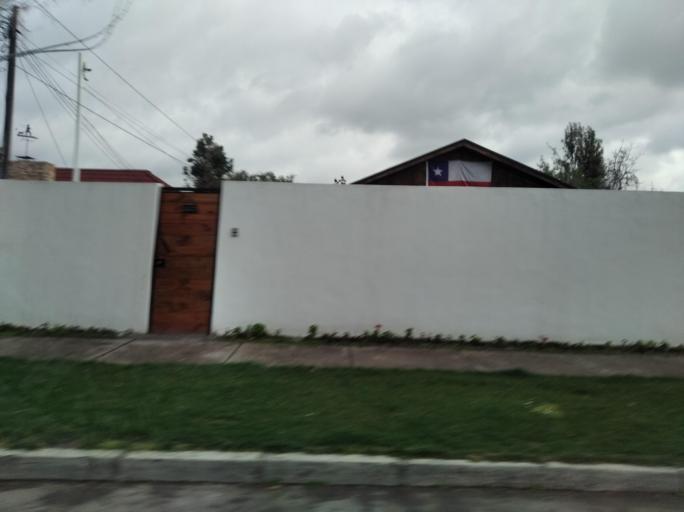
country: CL
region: Santiago Metropolitan
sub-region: Provincia de Santiago
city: Villa Presidente Frei, Nunoa, Santiago, Chile
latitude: -33.4880
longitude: -70.5943
